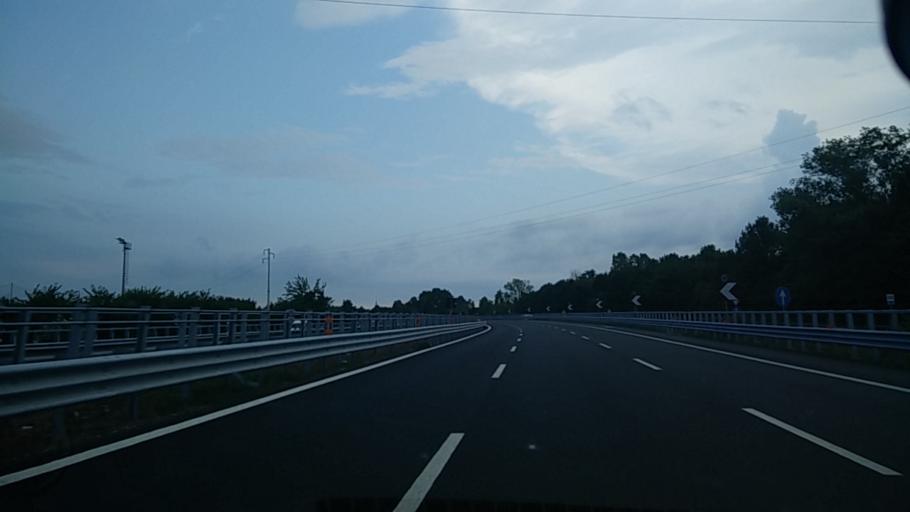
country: IT
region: Friuli Venezia Giulia
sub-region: Provincia di Udine
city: Colugna
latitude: 46.0846
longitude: 13.1920
